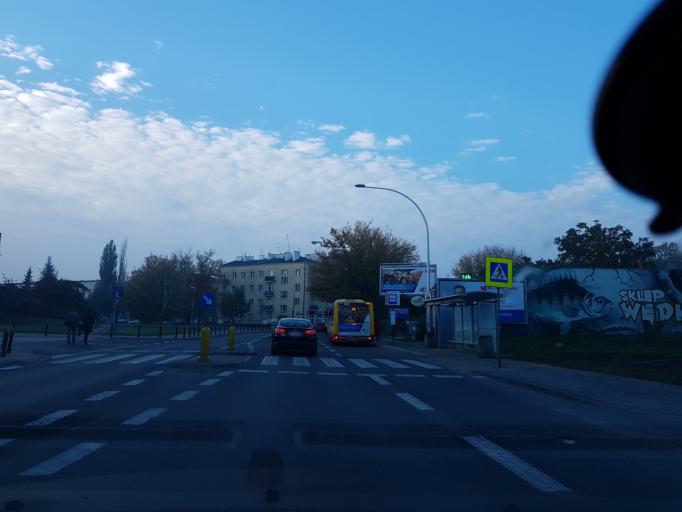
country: PL
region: Masovian Voivodeship
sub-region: Warszawa
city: Praga Polnoc
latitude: 52.2708
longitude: 21.0417
